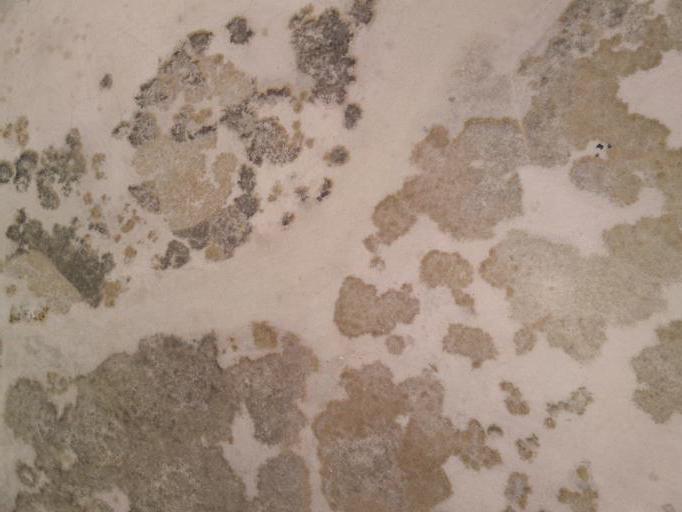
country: BO
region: La Paz
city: Batallas
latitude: -16.3510
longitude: -68.6301
